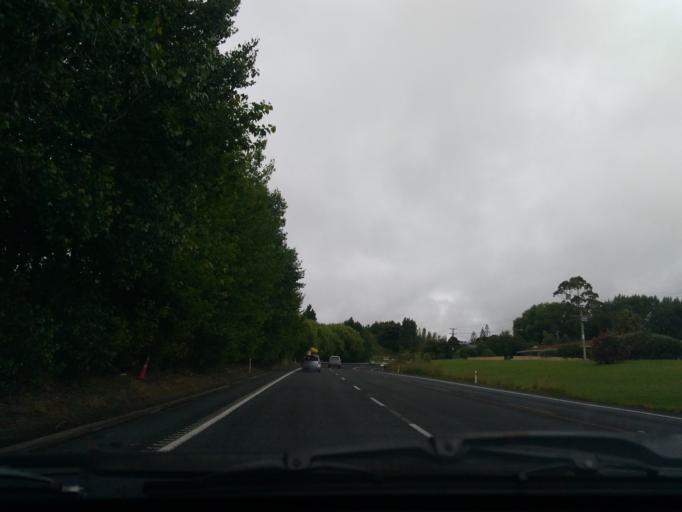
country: NZ
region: Auckland
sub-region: Auckland
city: Wellsford
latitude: -36.1542
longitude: 174.4396
